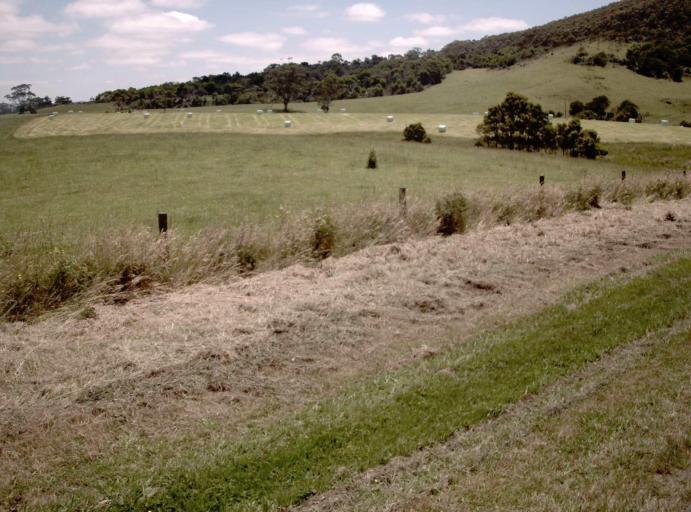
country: AU
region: Victoria
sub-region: Bass Coast
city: North Wonthaggi
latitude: -38.7171
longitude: 146.1097
